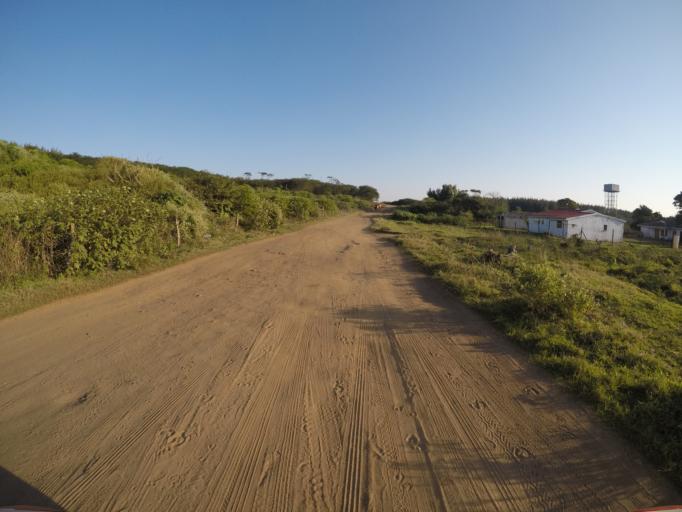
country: ZA
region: KwaZulu-Natal
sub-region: uThungulu District Municipality
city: KwaMbonambi
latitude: -28.7072
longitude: 32.1851
